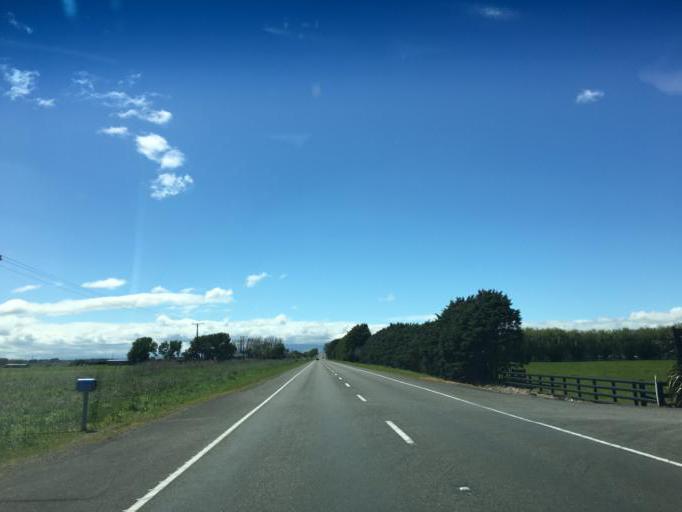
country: NZ
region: Manawatu-Wanganui
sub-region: Palmerston North City
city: Palmerston North
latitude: -40.3886
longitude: 175.5320
